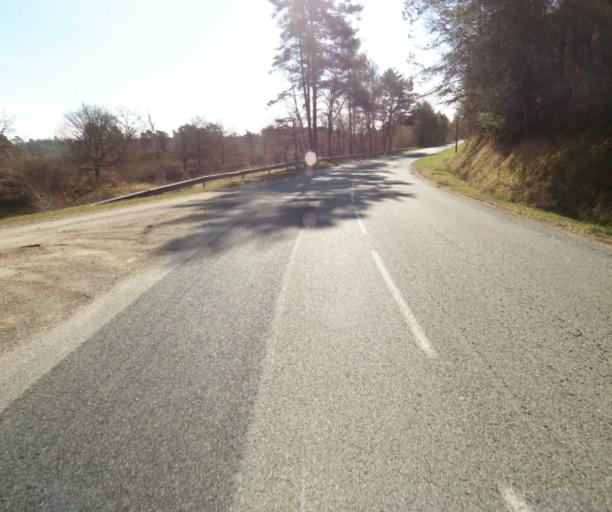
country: FR
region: Limousin
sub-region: Departement de la Correze
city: Correze
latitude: 45.2834
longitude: 1.9213
